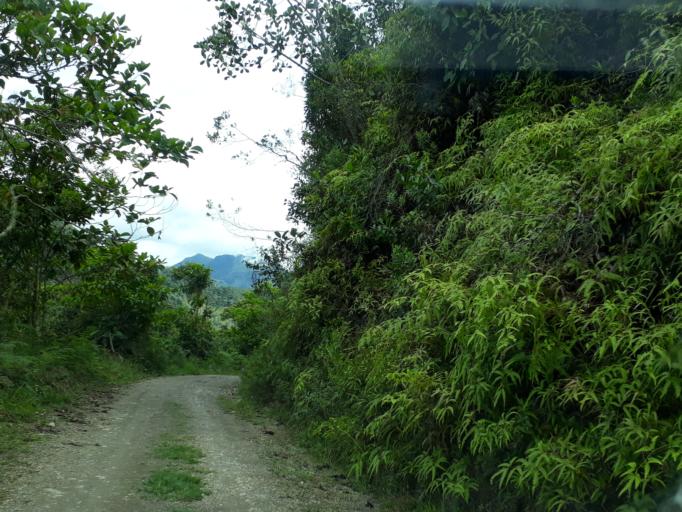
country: CO
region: Boyaca
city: Quipama
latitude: 5.3913
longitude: -74.1185
